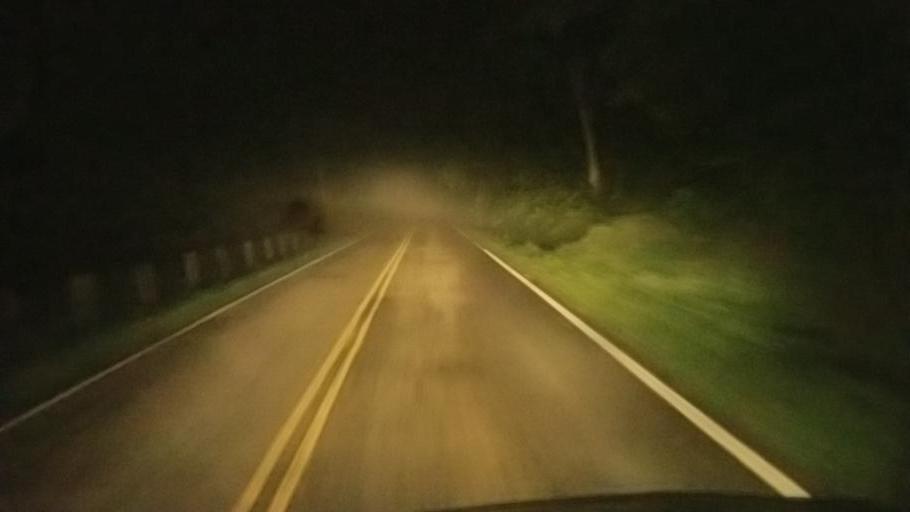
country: US
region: Ohio
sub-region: Coshocton County
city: Coshocton
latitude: 40.3610
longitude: -82.0289
